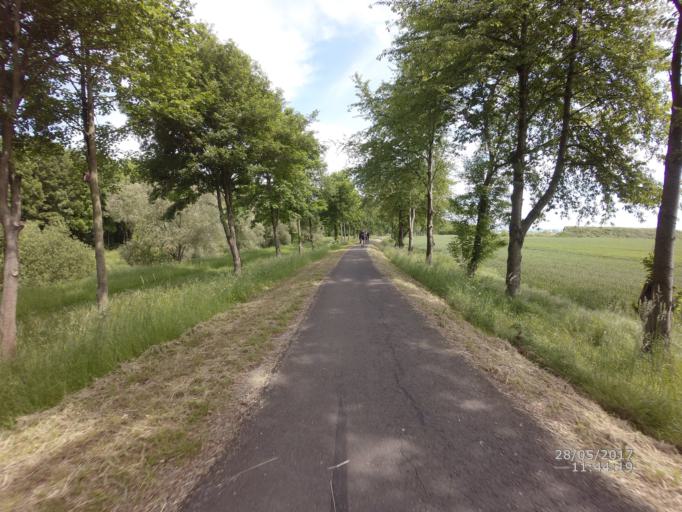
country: DE
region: Thuringia
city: Soemmerda
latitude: 51.1931
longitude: 11.1263
